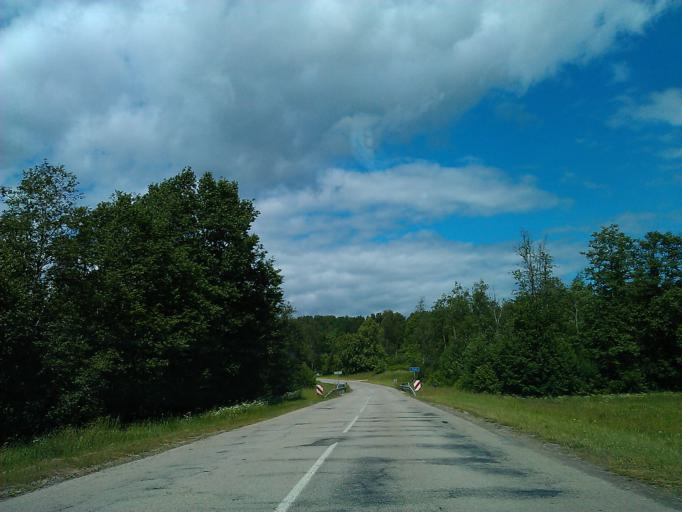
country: LV
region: Talsu Rajons
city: Sabile
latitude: 57.0833
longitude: 22.5257
